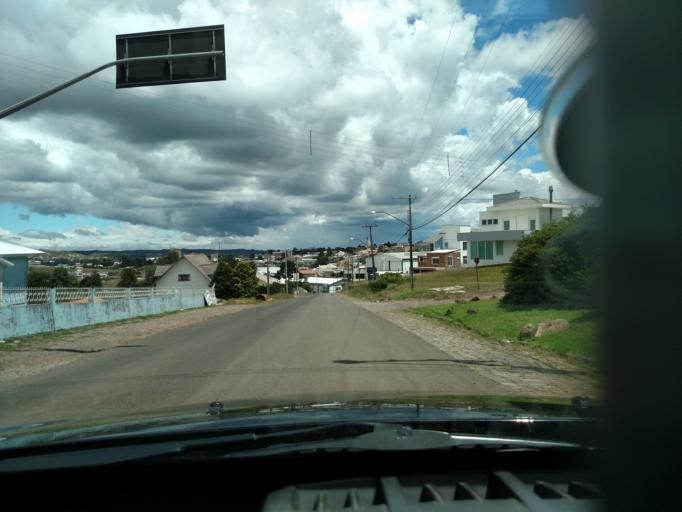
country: BR
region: Santa Catarina
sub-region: Sao Joaquim
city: Sao Joaquim
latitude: -28.2767
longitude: -49.9288
